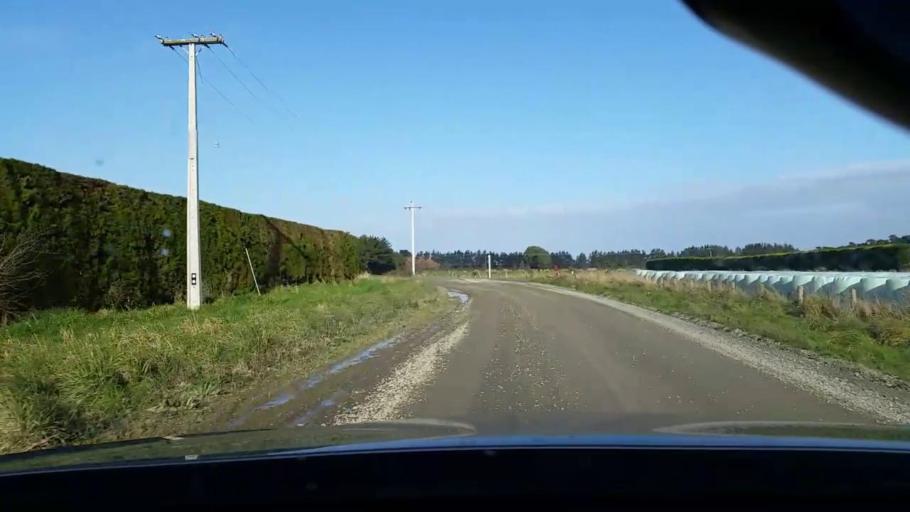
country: NZ
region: Southland
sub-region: Invercargill City
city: Invercargill
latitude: -46.2937
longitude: 168.2947
